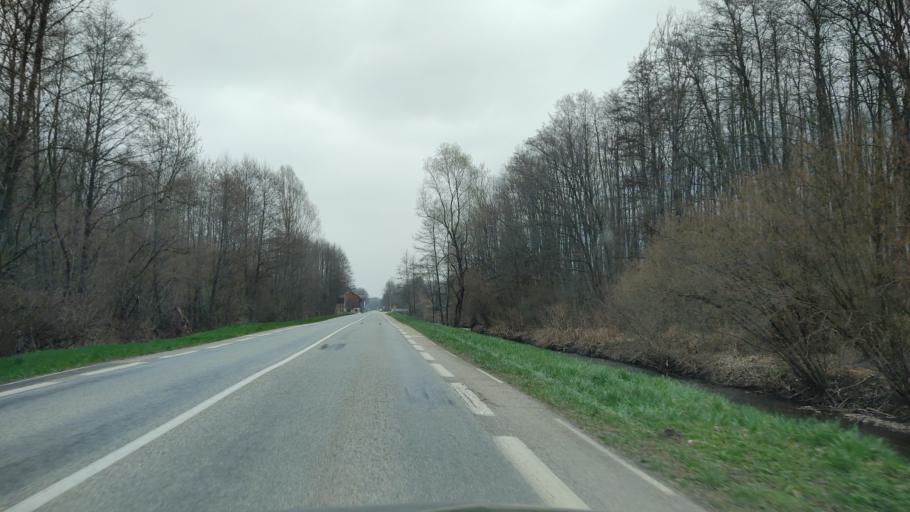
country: FR
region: Rhone-Alpes
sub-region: Departement de la Savoie
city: Coise-Saint-Jean-Pied-Gauthier
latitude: 45.4876
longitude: 6.1481
